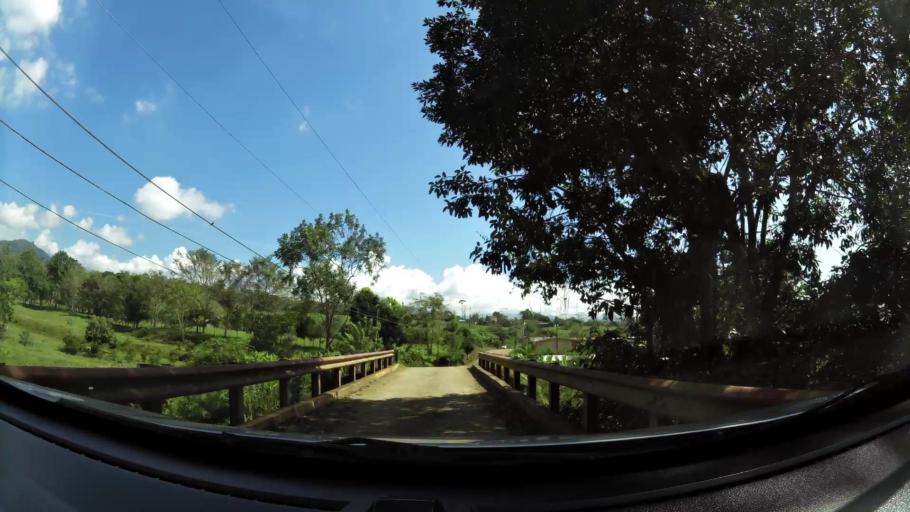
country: CR
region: San Jose
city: San Isidro
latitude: 9.3864
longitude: -83.7030
